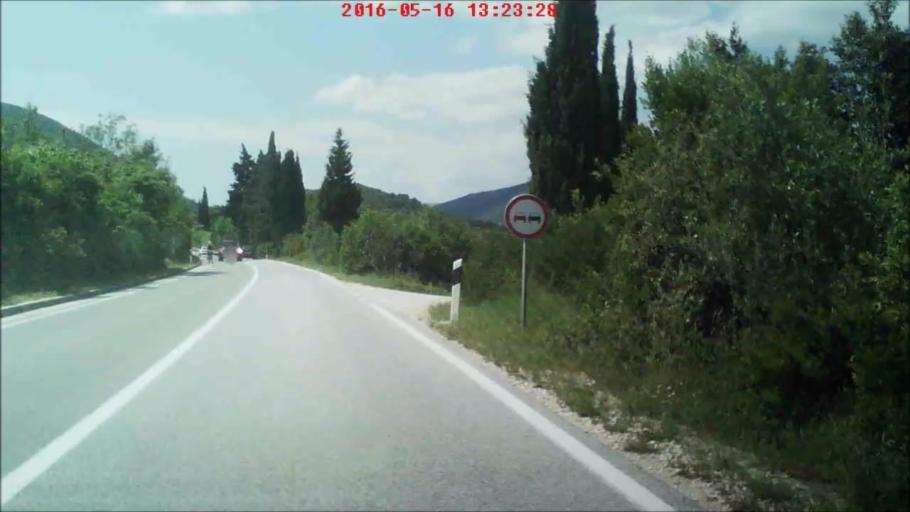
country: HR
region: Dubrovacko-Neretvanska
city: Ston
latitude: 42.8424
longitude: 17.7125
